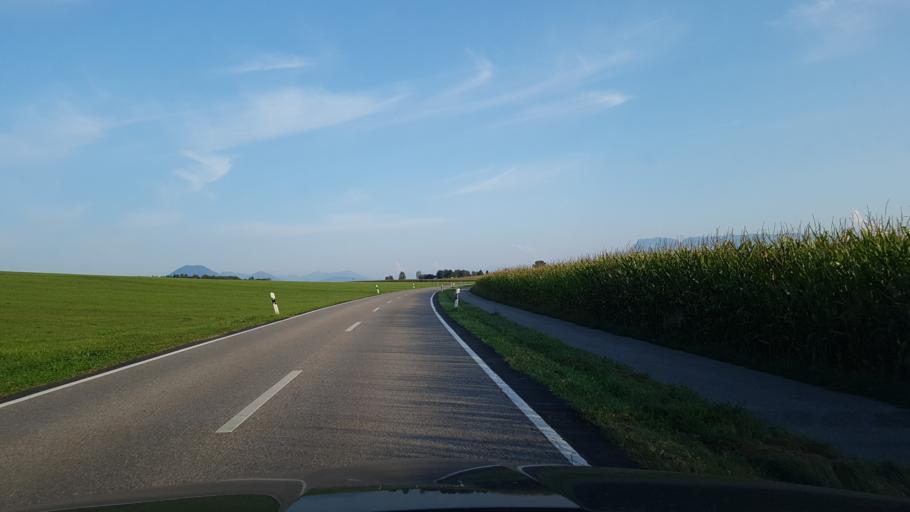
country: DE
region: Bavaria
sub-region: Upper Bavaria
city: Laufen
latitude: 47.8980
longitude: 12.9183
